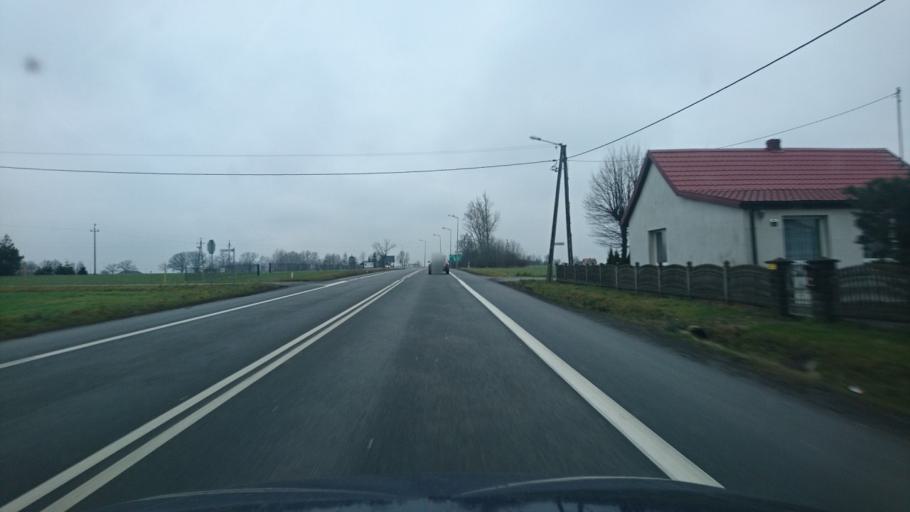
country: PL
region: Lodz Voivodeship
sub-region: Powiat wieruszowski
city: Walichnowy
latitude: 51.3038
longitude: 18.3804
